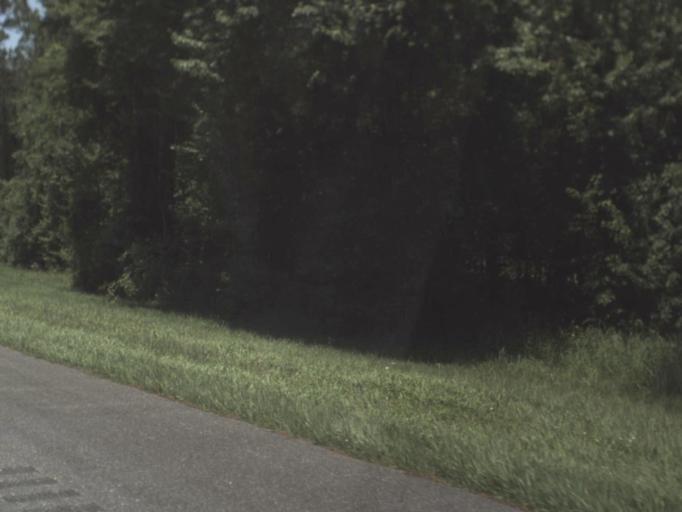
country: US
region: Florida
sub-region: Columbia County
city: Watertown
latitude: 30.2570
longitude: -82.4554
